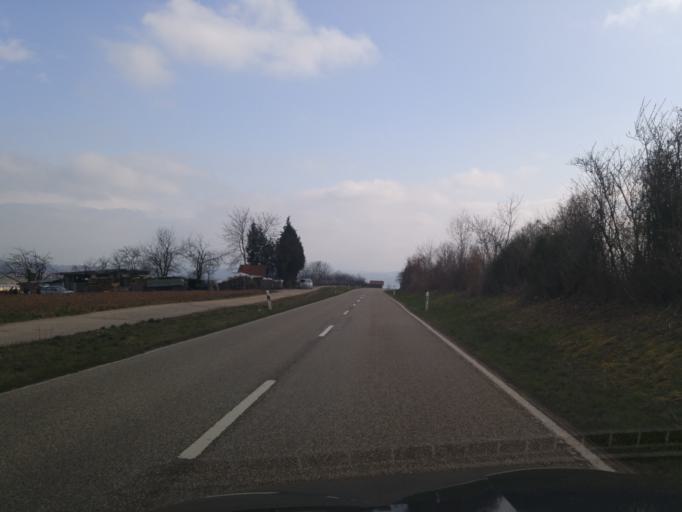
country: DE
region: Baden-Wuerttemberg
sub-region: Regierungsbezirk Stuttgart
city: Ilsfeld
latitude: 49.0691
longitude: 9.2397
